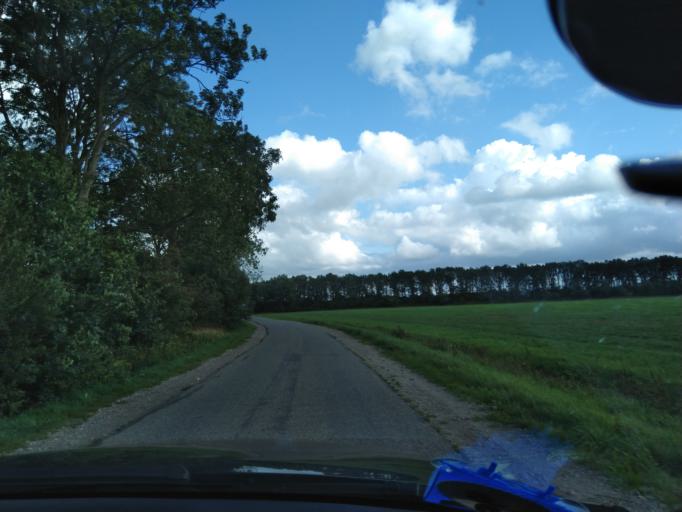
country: NL
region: Drenthe
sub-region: Gemeente Tynaarlo
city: Vries
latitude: 53.0827
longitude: 6.5395
